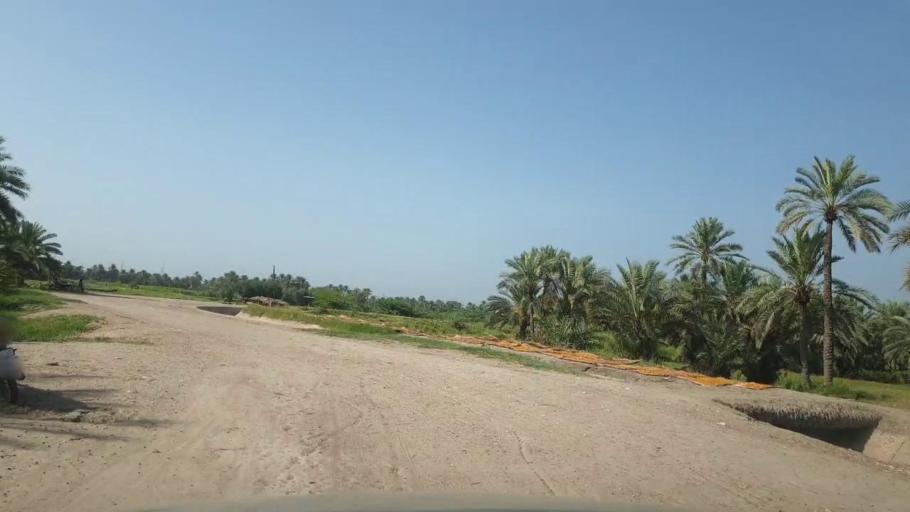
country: PK
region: Sindh
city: Rohri
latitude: 27.6587
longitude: 68.8838
